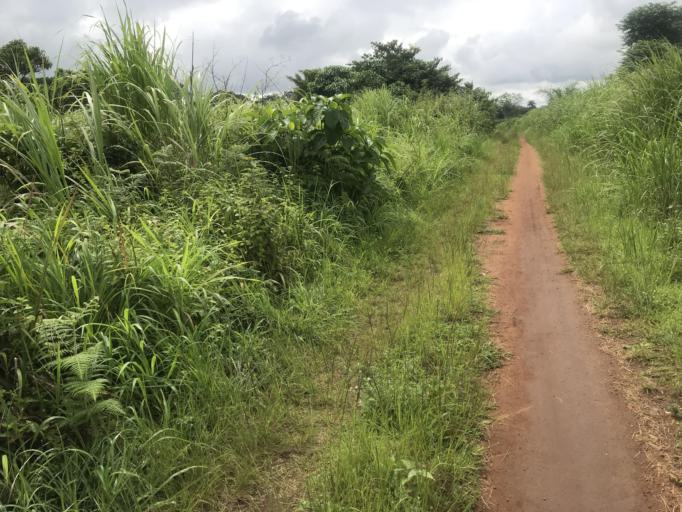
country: SL
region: Eastern Province
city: Buedu
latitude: 8.4630
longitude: -10.3129
